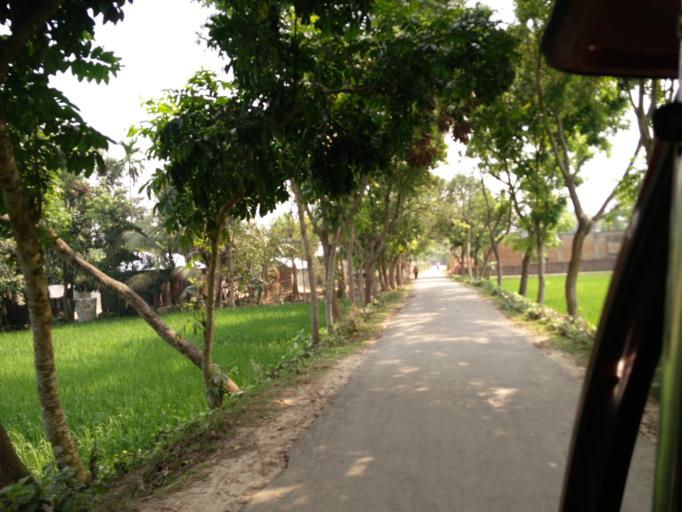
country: BD
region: Dhaka
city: Muktagacha
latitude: 24.9191
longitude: 90.2361
